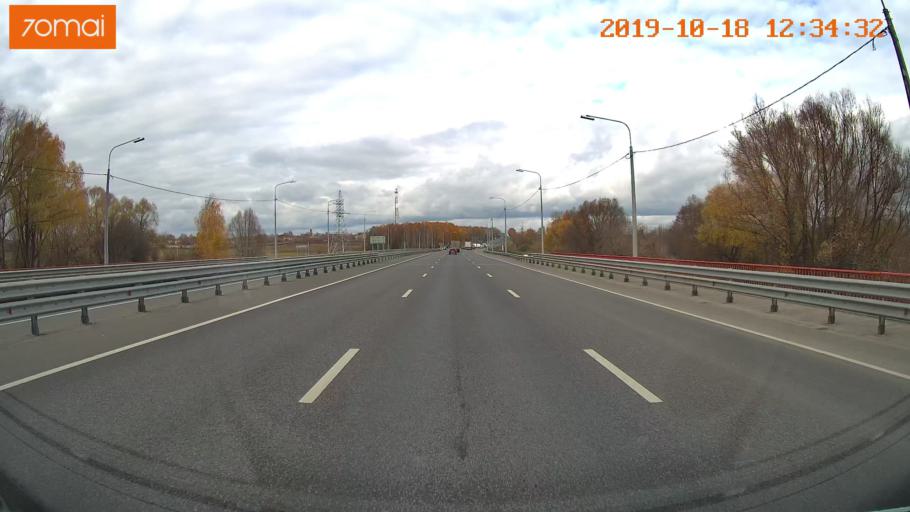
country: RU
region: Rjazan
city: Ryazan'
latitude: 54.6150
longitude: 39.6379
